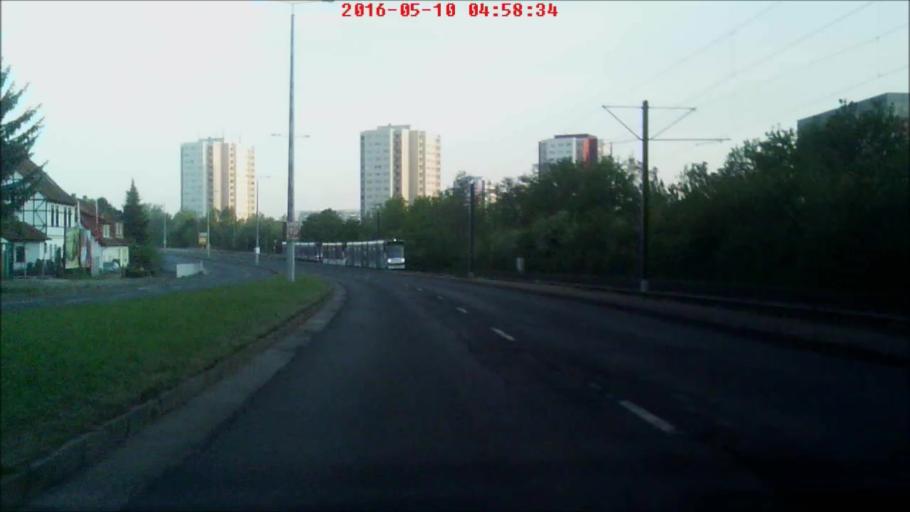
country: DE
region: Thuringia
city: Erfurt
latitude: 51.0036
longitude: 11.0026
